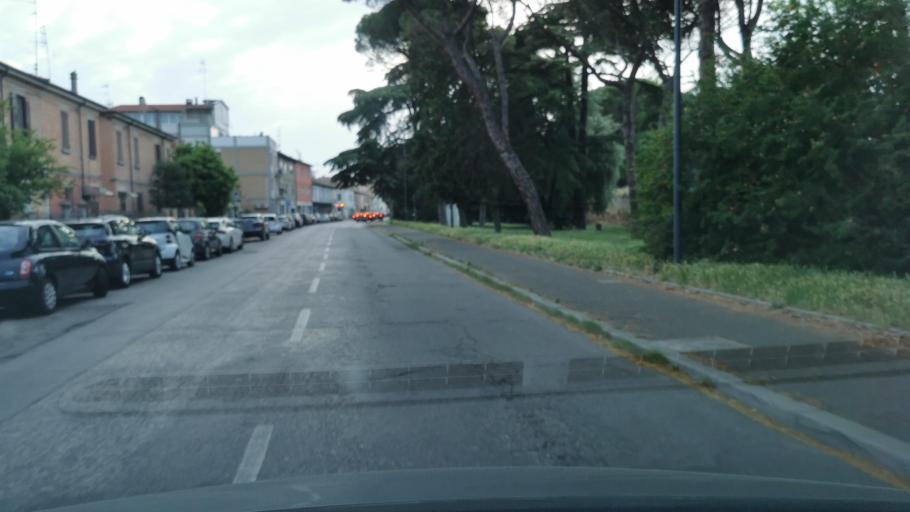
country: IT
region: Emilia-Romagna
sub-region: Provincia di Ravenna
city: Ravenna
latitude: 44.4127
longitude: 12.1940
